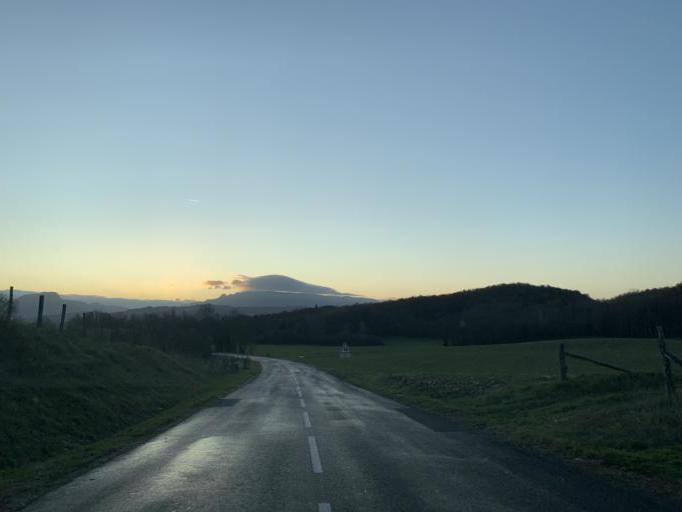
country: FR
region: Rhone-Alpes
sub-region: Departement de l'Ain
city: Belley
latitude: 45.7896
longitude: 5.6453
